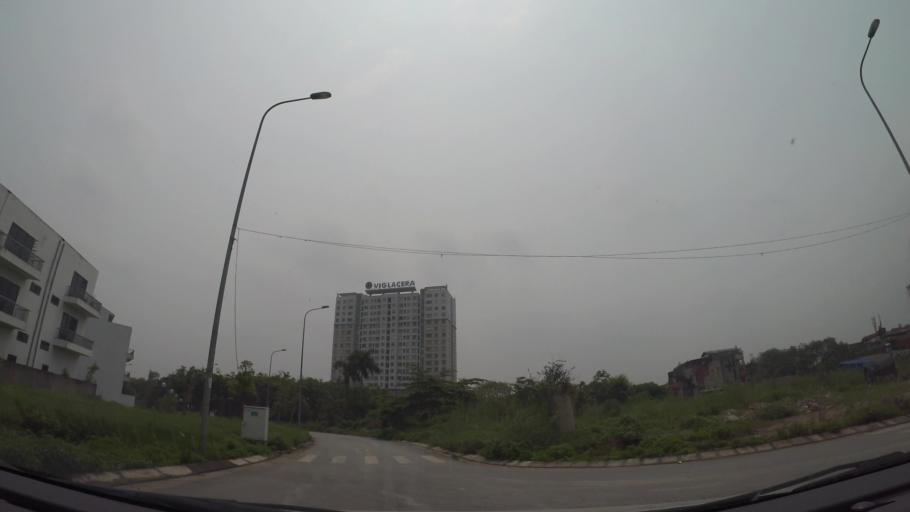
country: VN
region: Ha Noi
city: Cau Dien
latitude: 21.0282
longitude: 105.7422
